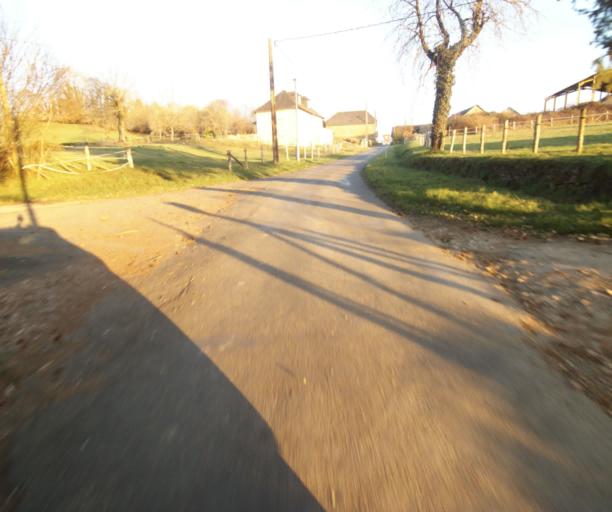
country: FR
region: Limousin
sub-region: Departement de la Correze
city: Saint-Clement
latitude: 45.3656
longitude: 1.6202
